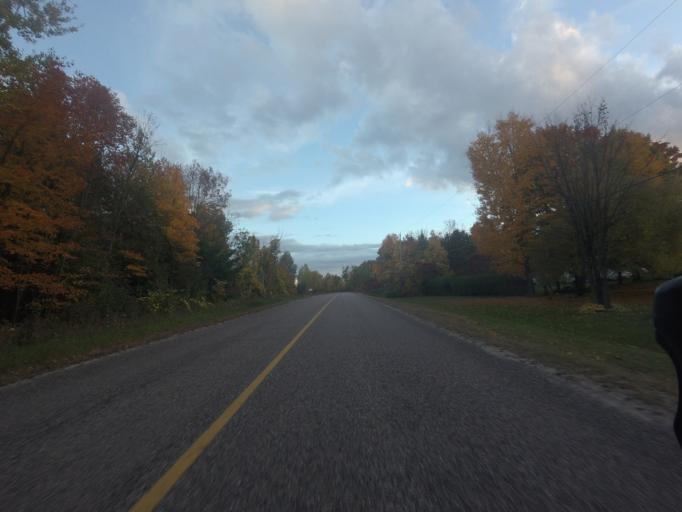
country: CA
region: Ontario
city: Renfrew
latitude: 45.4135
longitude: -76.9539
